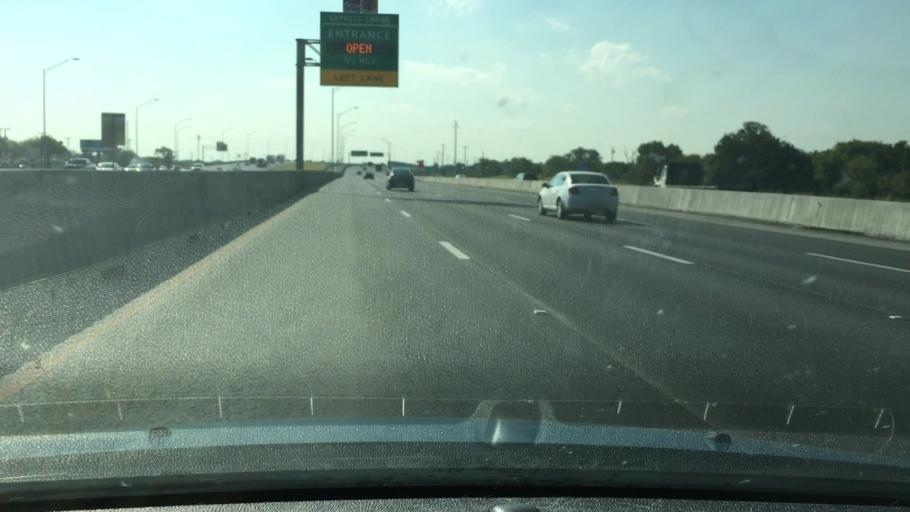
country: US
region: Texas
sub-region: Denton County
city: Lake Dallas
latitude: 33.1181
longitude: -97.0318
